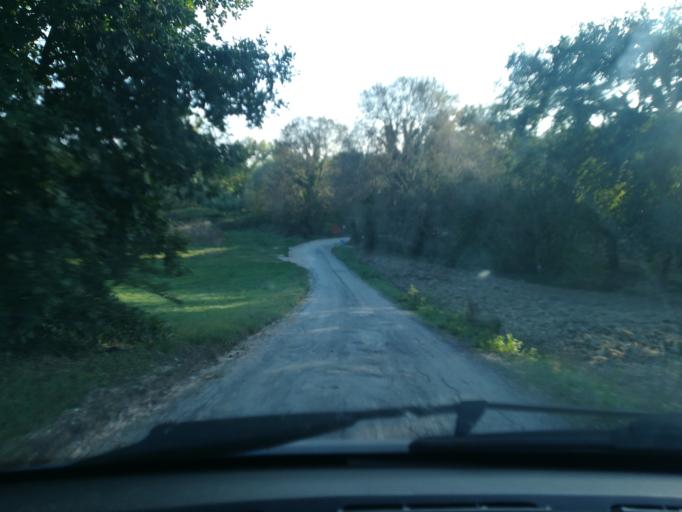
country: IT
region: The Marches
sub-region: Provincia di Macerata
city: Macerata
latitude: 43.2837
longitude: 13.4551
